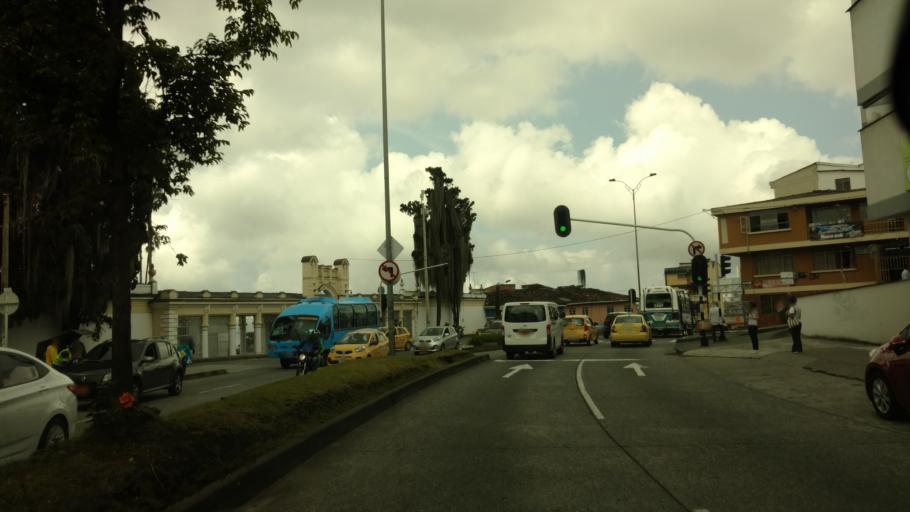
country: CO
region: Caldas
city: Manizales
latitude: 5.0642
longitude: -75.5029
